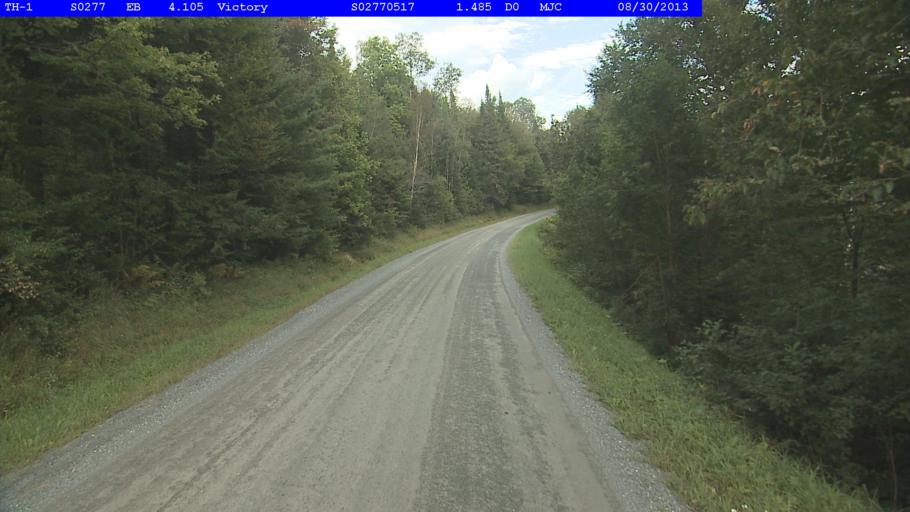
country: US
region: Vermont
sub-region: Caledonia County
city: Lyndonville
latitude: 44.5123
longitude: -71.8365
